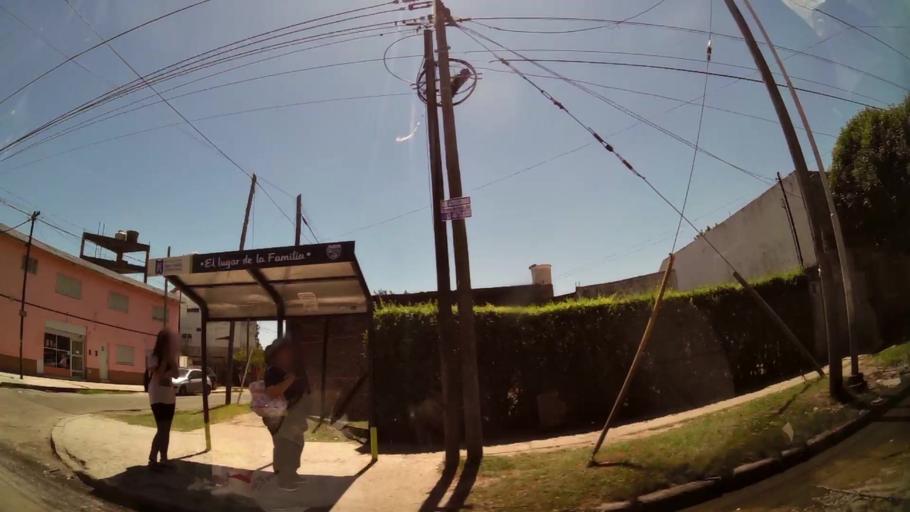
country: AR
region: Buenos Aires
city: Hurlingham
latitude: -34.4924
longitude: -58.6694
